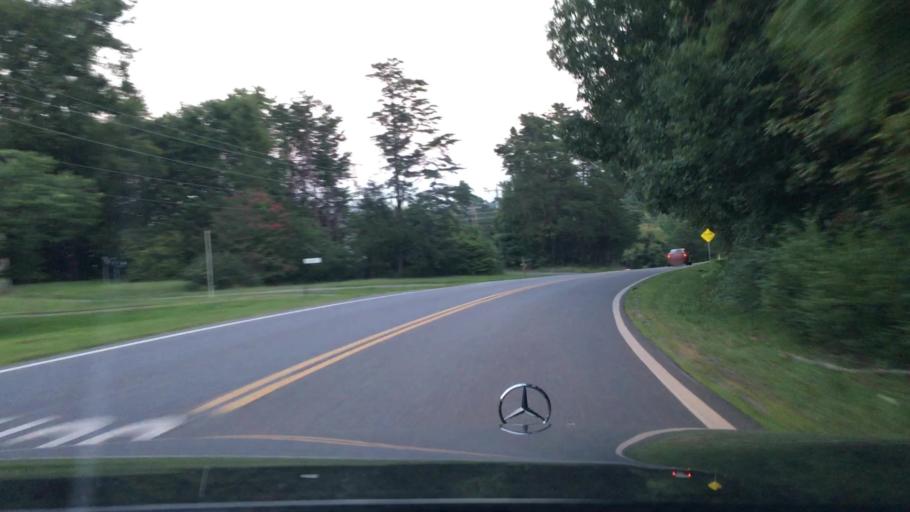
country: US
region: Virginia
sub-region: Campbell County
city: Altavista
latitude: 37.1304
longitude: -79.2801
